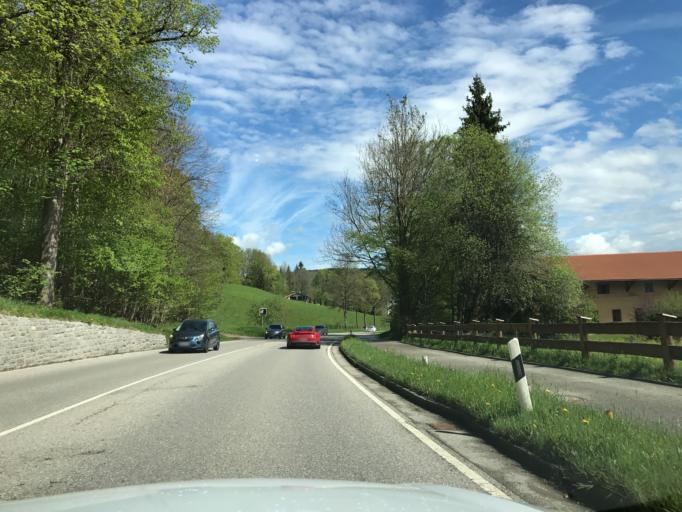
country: DE
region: Bavaria
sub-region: Upper Bavaria
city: Bad Wiessee
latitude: 47.7292
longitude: 11.7160
